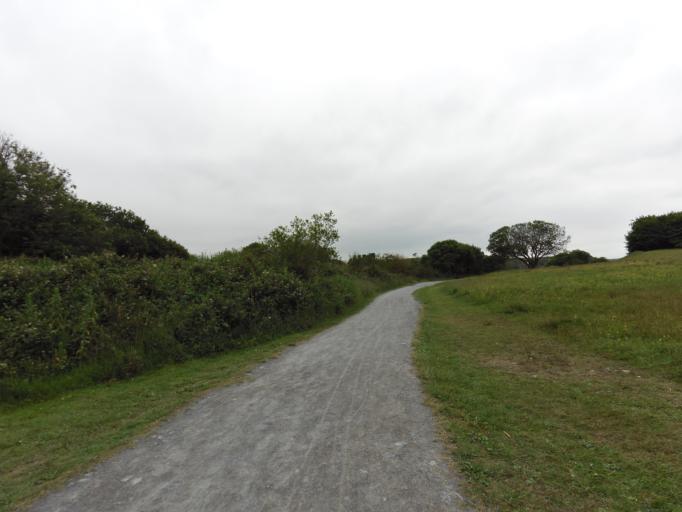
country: IE
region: Connaught
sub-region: County Galway
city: Gaillimh
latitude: 53.2961
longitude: -9.0770
